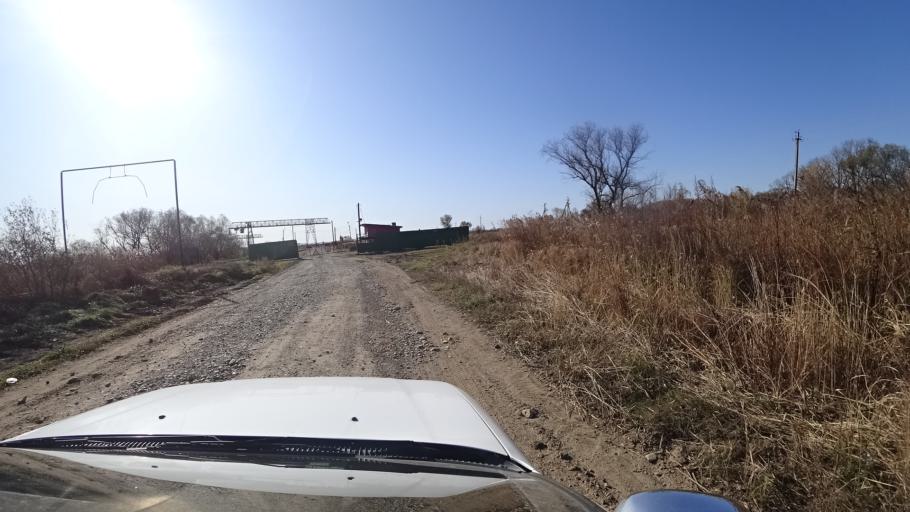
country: RU
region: Primorskiy
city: Dal'nerechensk
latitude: 45.9060
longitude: 133.7960
